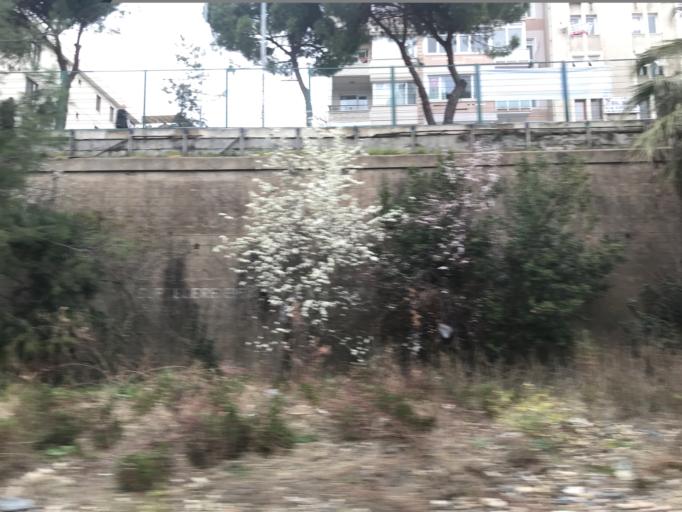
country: TR
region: Istanbul
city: Bahcelievler
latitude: 40.9807
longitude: 28.8728
